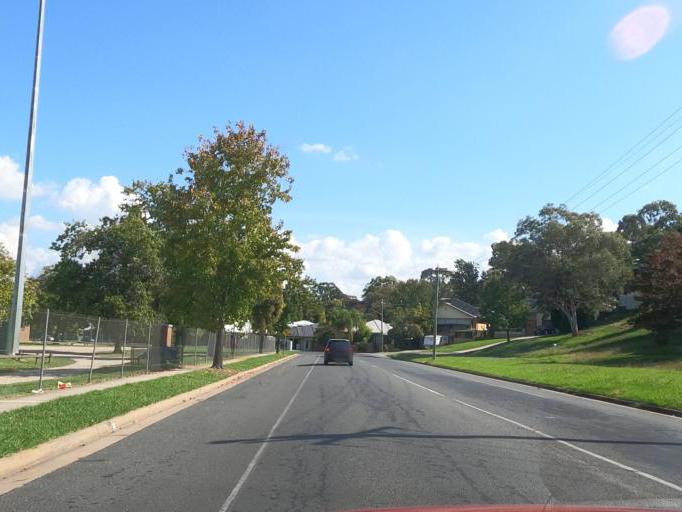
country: AU
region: New South Wales
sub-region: Albury Municipality
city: Albury
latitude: -36.0675
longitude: 146.9213
